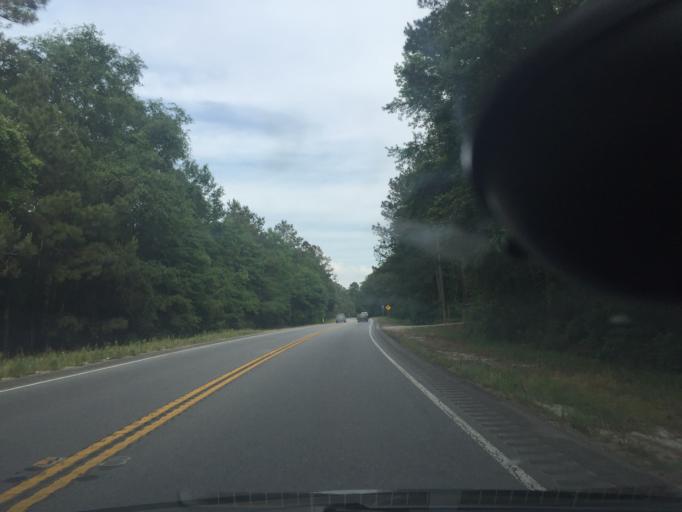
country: US
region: Georgia
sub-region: Bryan County
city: Richmond Hill
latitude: 32.0158
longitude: -81.3023
